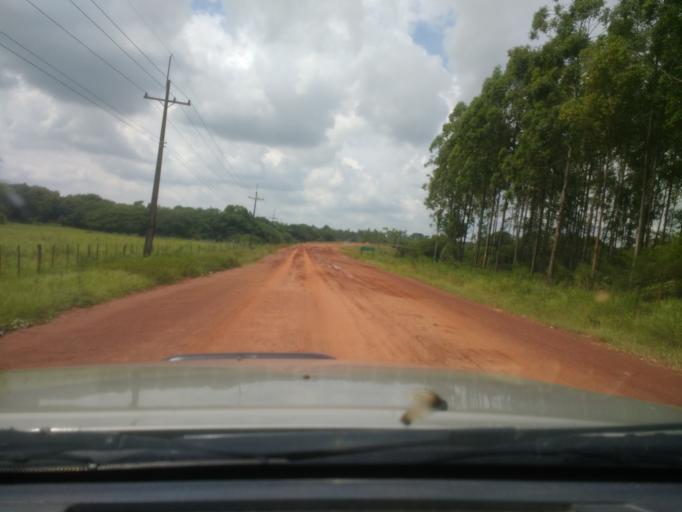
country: PY
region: San Pedro
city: Puerto Rosario
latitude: -24.4050
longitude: -57.1037
